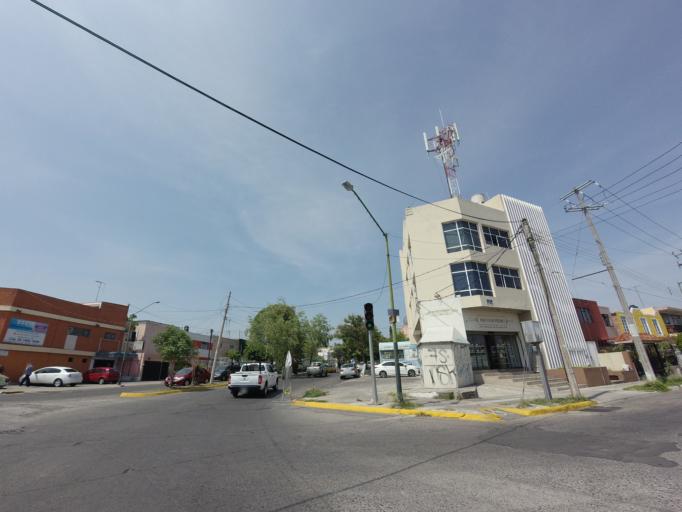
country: MX
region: Jalisco
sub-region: Zapopan
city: Zapopan
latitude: 20.6931
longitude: -103.3427
